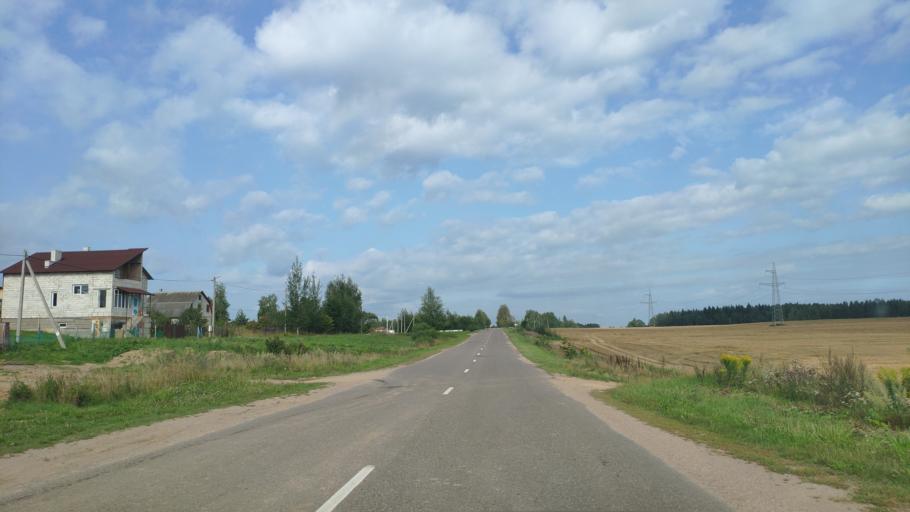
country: BY
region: Minsk
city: Khatsyezhyna
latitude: 53.8714
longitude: 27.3086
